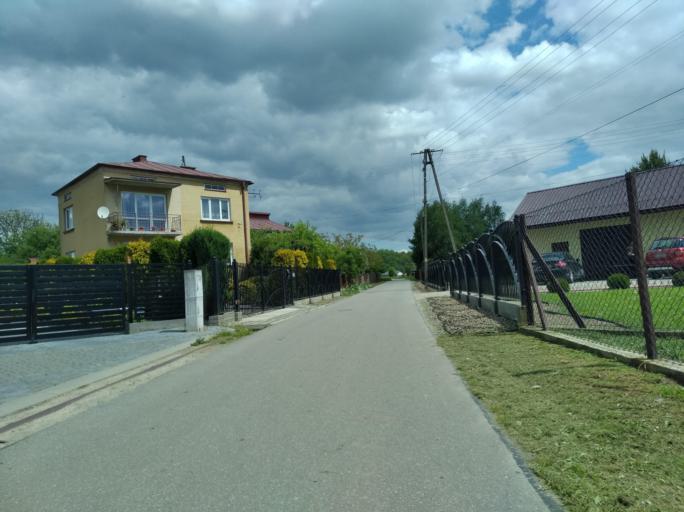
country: PL
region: Subcarpathian Voivodeship
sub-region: Powiat brzozowski
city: Jasionow
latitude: 49.6621
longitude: 21.9883
